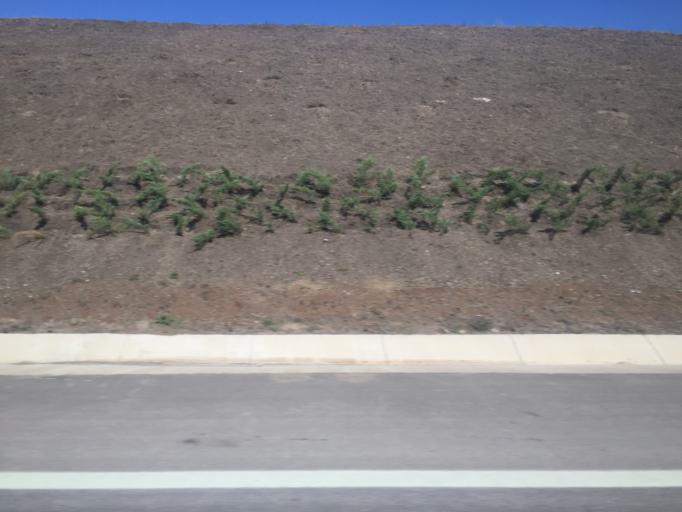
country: TR
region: Bursa
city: Karacabey
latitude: 40.2632
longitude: 28.4868
